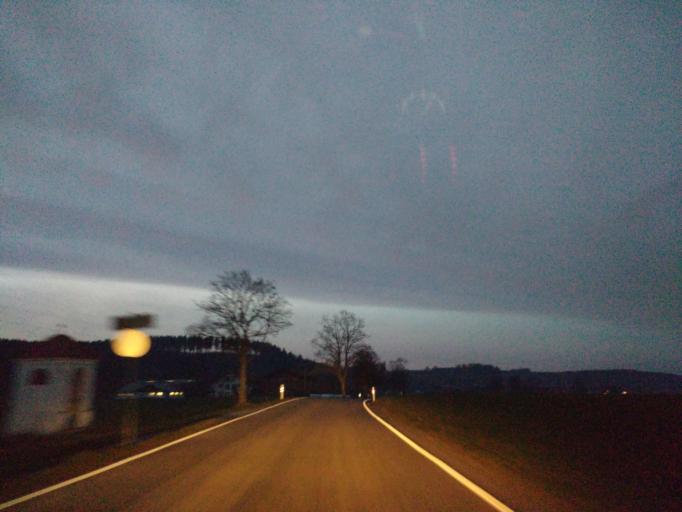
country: DE
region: Bavaria
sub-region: Swabia
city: Stottwang
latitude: 47.8643
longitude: 10.6926
